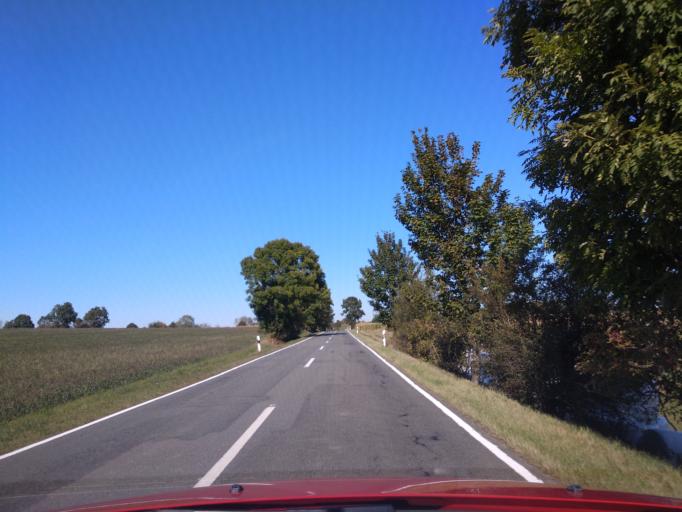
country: DE
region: Lower Saxony
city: Boffzen
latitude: 51.7362
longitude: 9.2978
